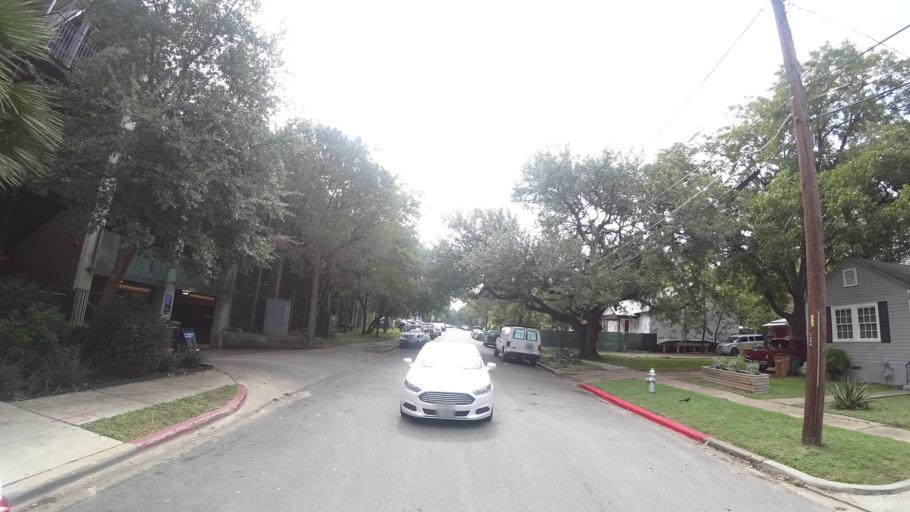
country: US
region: Texas
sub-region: Travis County
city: Austin
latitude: 30.2501
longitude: -97.7508
